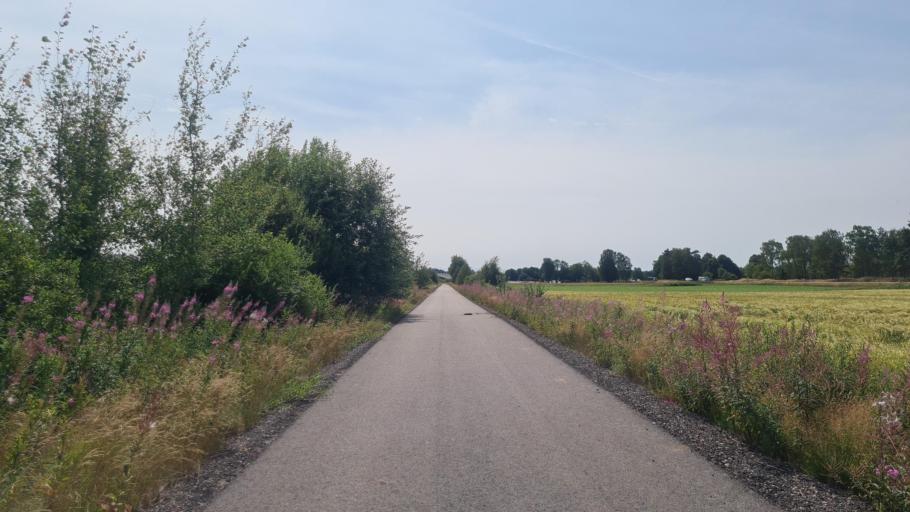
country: SE
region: Kronoberg
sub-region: Ljungby Kommun
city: Lagan
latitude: 56.8786
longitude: 13.9839
